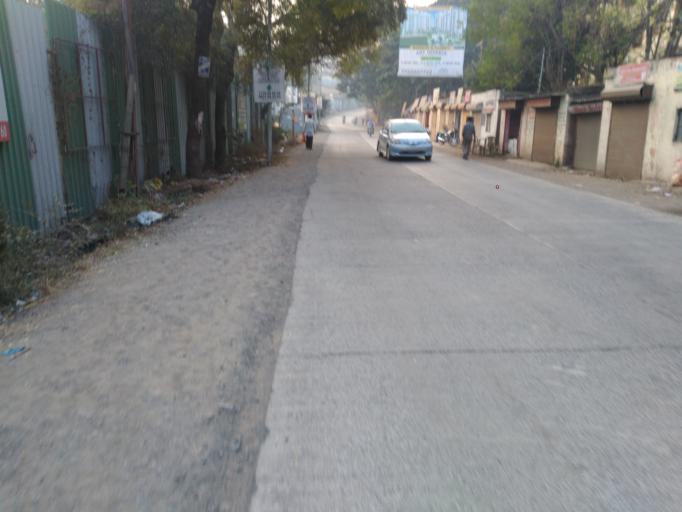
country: IN
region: Maharashtra
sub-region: Pune Division
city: Pune
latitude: 18.4537
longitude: 73.9147
